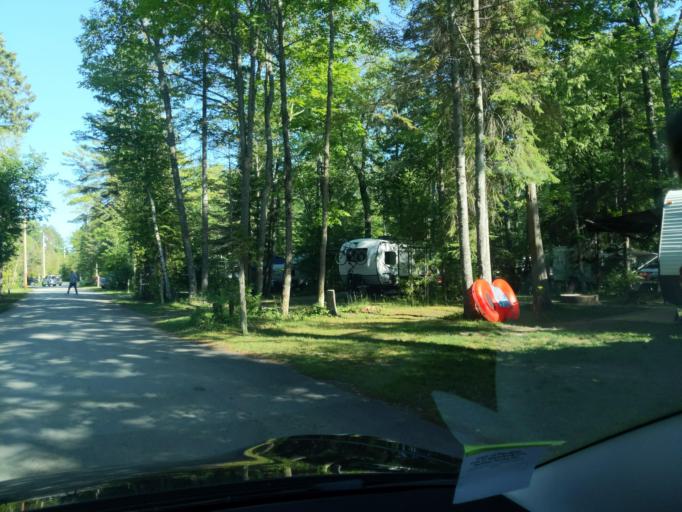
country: US
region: Michigan
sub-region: Mackinac County
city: Saint Ignace
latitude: 45.7506
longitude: -84.6836
